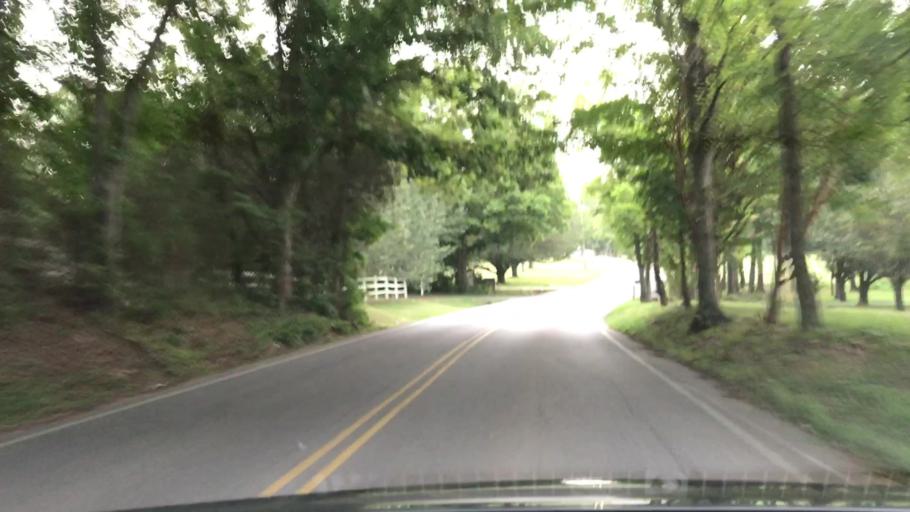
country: US
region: Tennessee
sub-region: Williamson County
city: Nolensville
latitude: 35.9765
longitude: -86.6572
